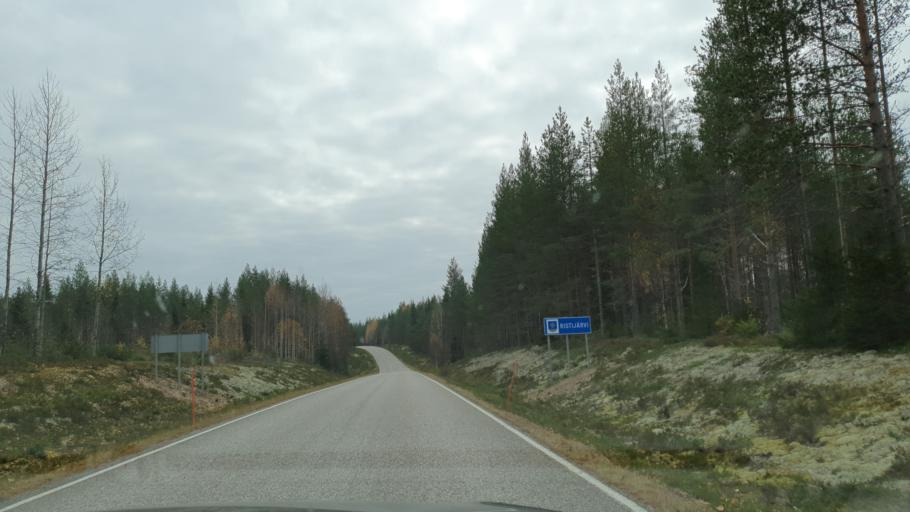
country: FI
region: Kainuu
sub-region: Kajaani
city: Ristijaervi
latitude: 64.6192
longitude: 27.9942
